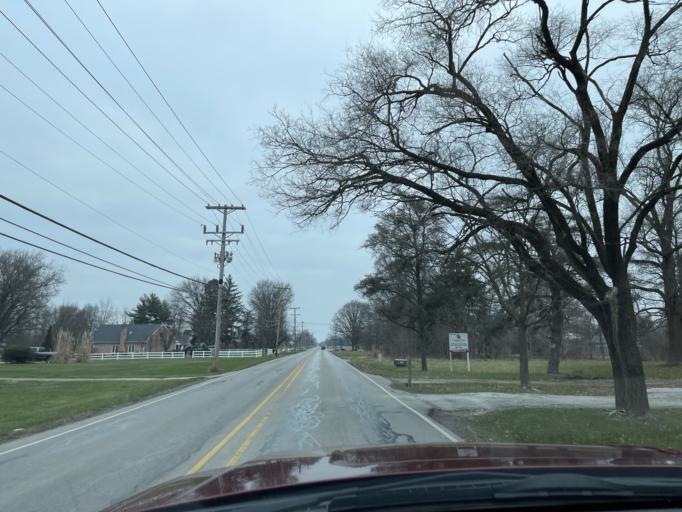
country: US
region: Indiana
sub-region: Hendricks County
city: Avon
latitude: 39.7975
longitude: -86.4005
